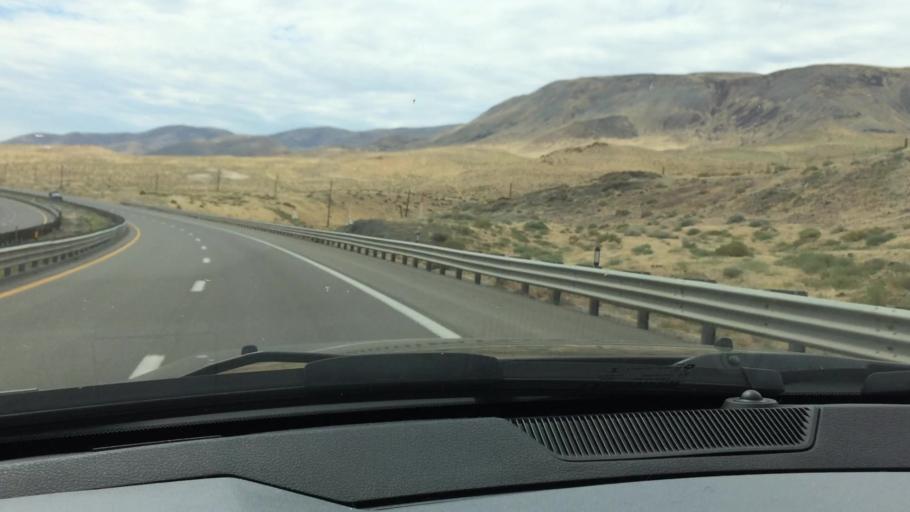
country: US
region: Nevada
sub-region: Lyon County
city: Fernley
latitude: 39.5910
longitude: -119.3809
